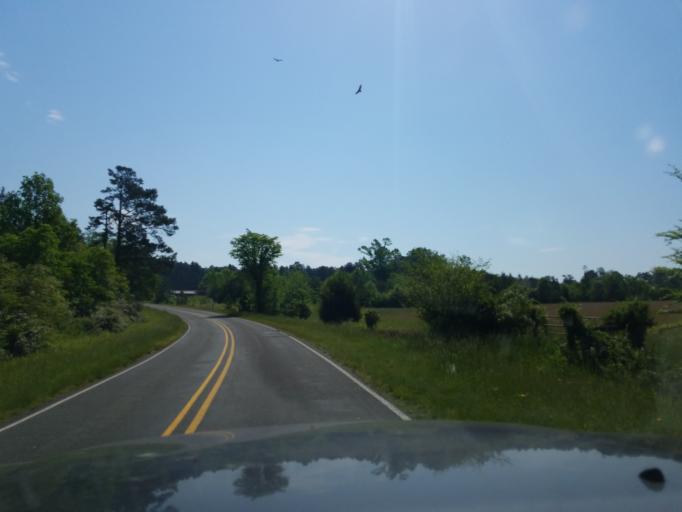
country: US
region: North Carolina
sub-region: Vance County
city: Henderson
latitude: 36.3983
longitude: -78.4251
